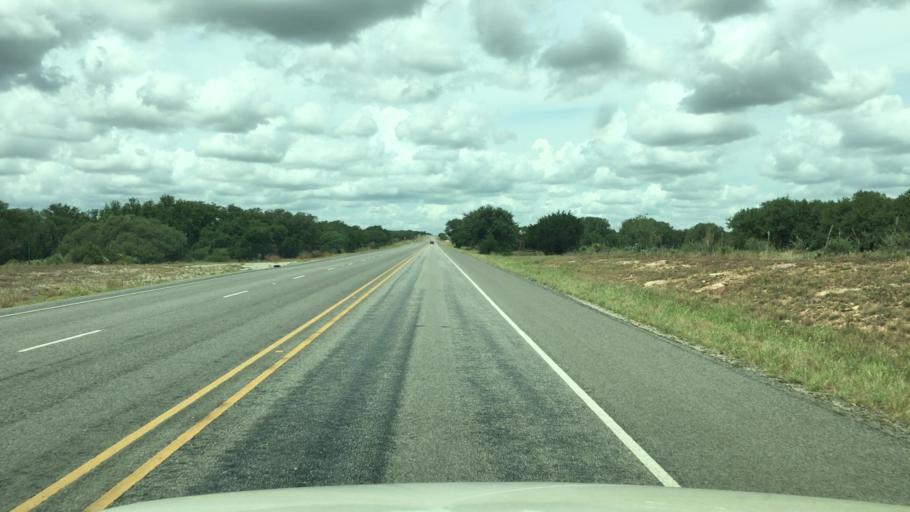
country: US
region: Texas
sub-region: McCulloch County
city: Brady
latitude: 31.0247
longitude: -99.2209
